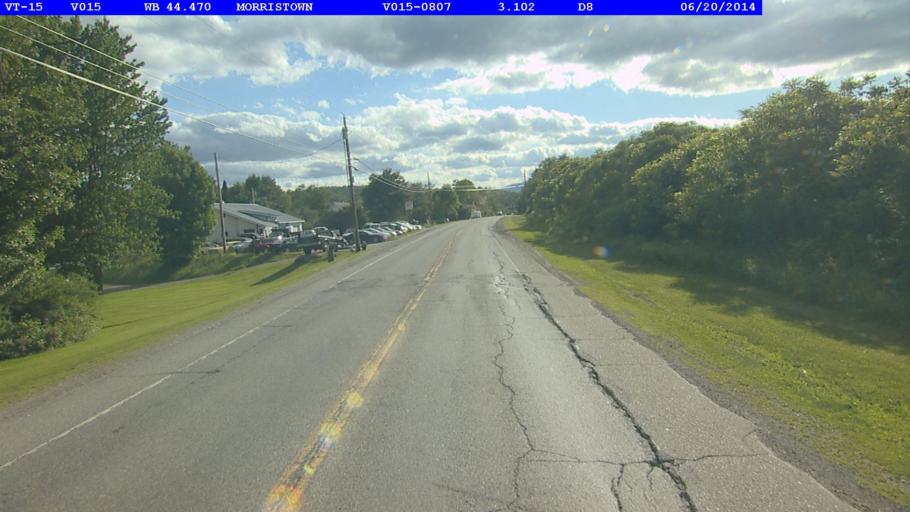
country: US
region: Vermont
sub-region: Lamoille County
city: Morrisville
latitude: 44.5669
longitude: -72.5526
